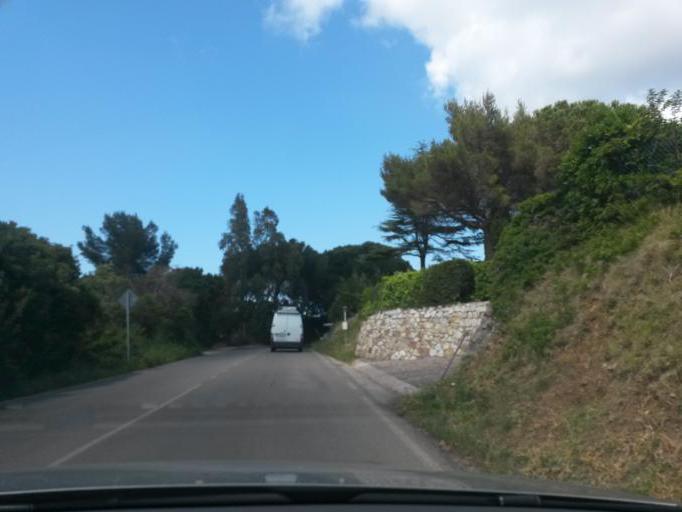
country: IT
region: Tuscany
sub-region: Provincia di Livorno
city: Campo nell'Elba
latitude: 42.7876
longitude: 10.2383
